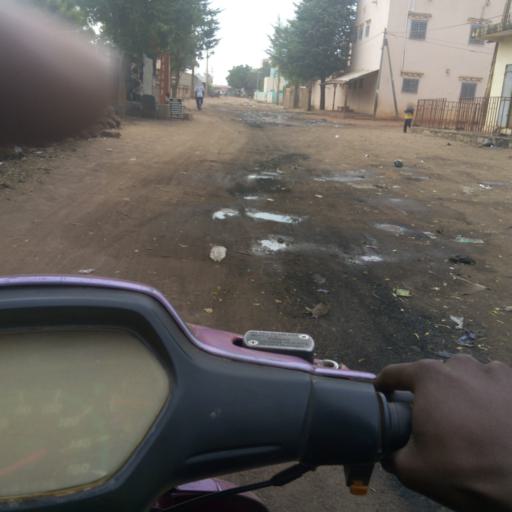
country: ML
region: Bamako
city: Bamako
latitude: 12.6658
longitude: -7.9451
